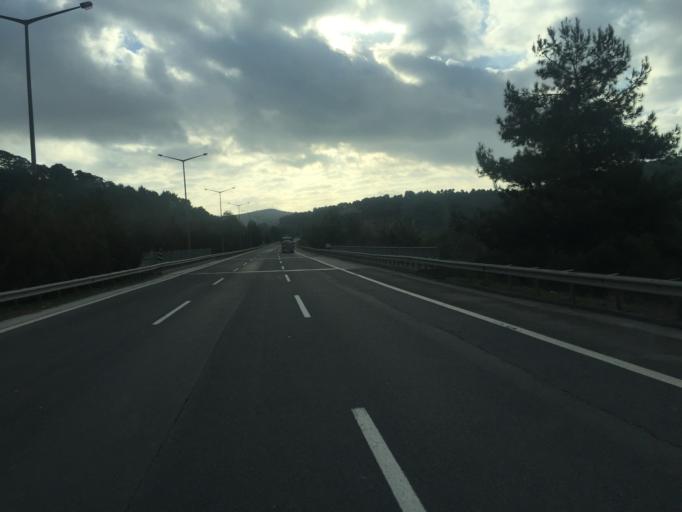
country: TR
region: Mersin
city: Camliyayla
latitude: 37.2019
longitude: 34.8191
